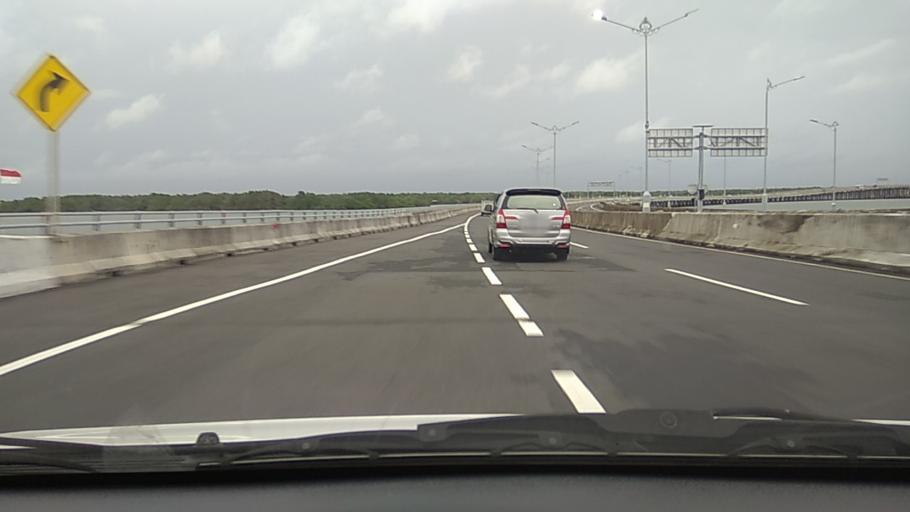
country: ID
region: Bali
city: Kelanabian
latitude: -8.7425
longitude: 115.1962
